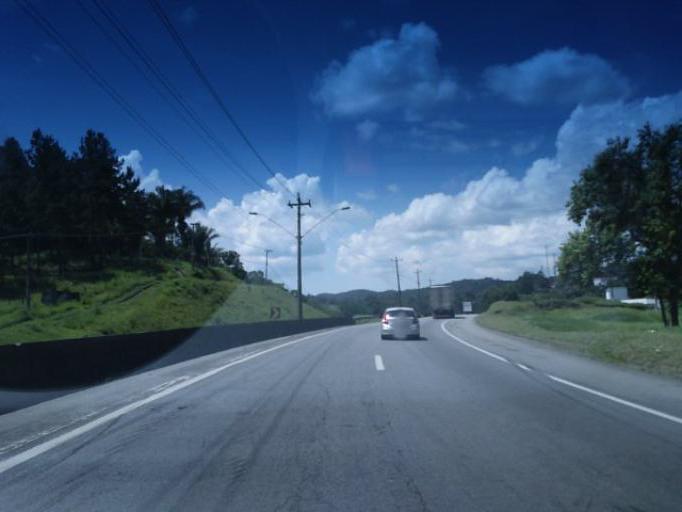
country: BR
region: Sao Paulo
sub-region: Sao Lourenco Da Serra
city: Sao Lourenco da Serra
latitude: -23.9150
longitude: -46.9892
